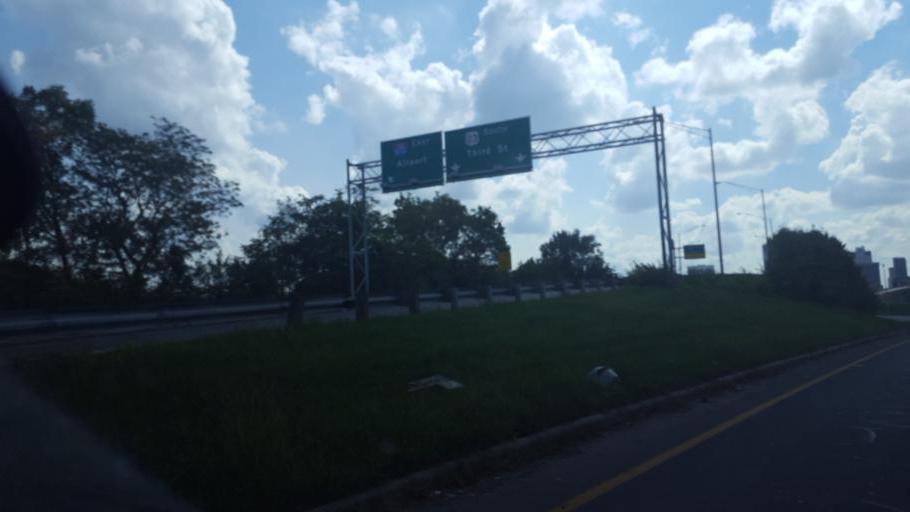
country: US
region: Ohio
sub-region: Franklin County
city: Columbus
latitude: 39.9771
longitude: -83.0003
